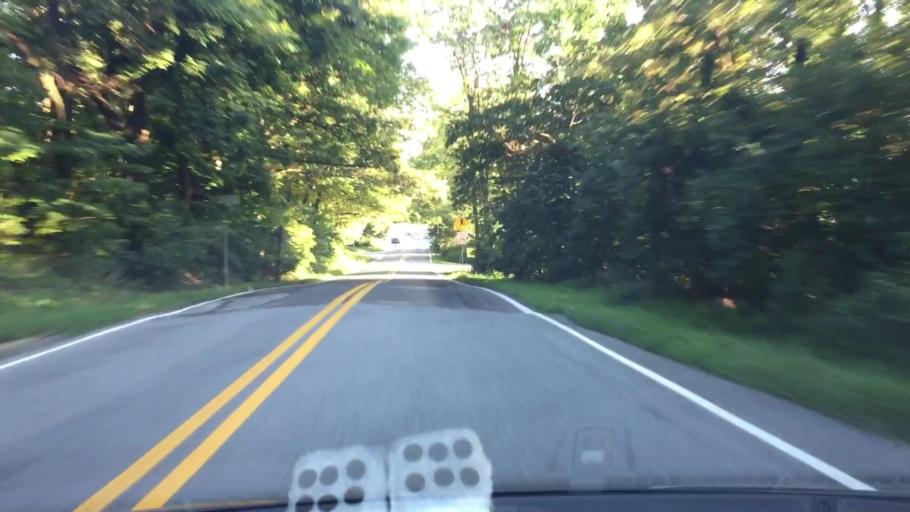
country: US
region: Pennsylvania
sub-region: Delaware County
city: Boothwyn
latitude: 39.8180
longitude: -75.4458
